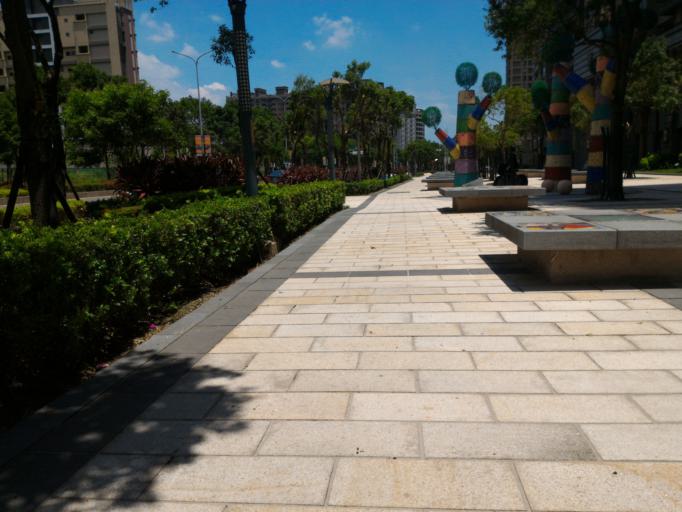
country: TW
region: Taiwan
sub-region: Taoyuan
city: Taoyuan
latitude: 24.9480
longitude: 121.3805
